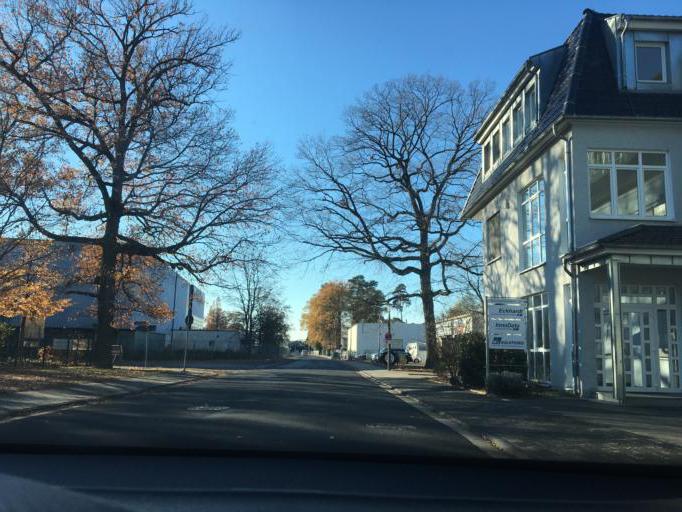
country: DE
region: Hesse
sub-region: Regierungsbezirk Darmstadt
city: Langenselbold
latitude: 50.1644
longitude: 9.0568
